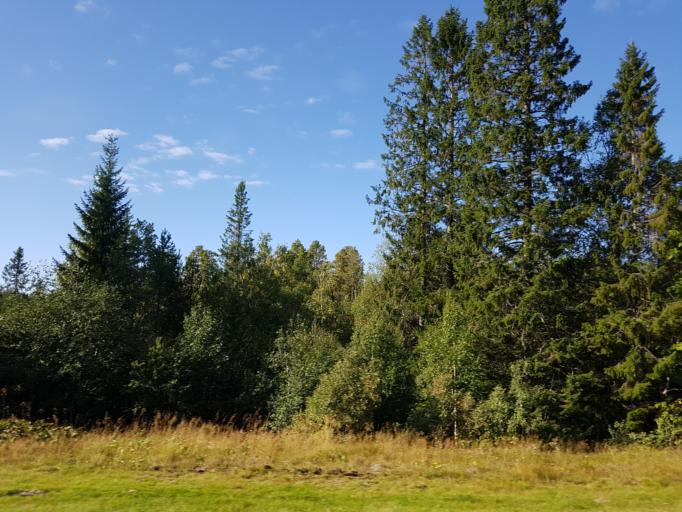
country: NO
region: Sor-Trondelag
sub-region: Trondheim
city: Trondheim
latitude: 63.6459
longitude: 10.2674
